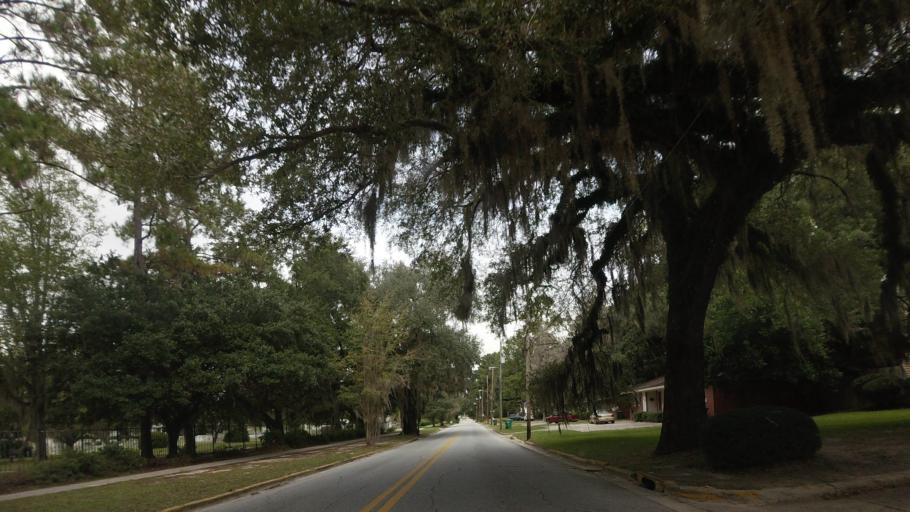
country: US
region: Georgia
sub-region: Lowndes County
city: Valdosta
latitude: 30.8414
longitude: -83.2876
